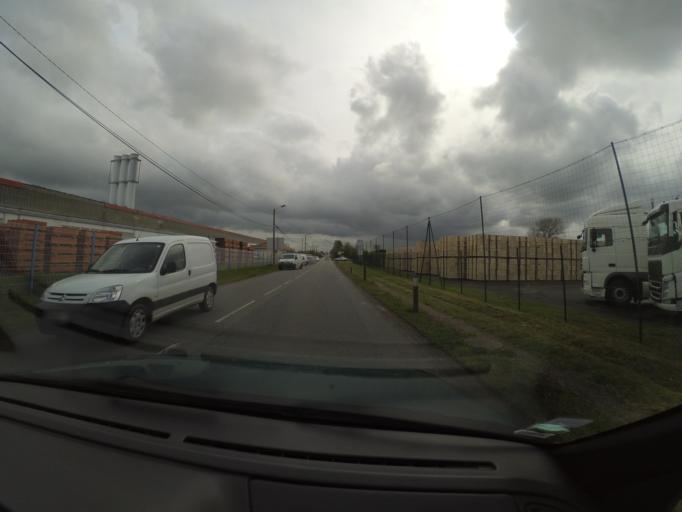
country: FR
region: Pays de la Loire
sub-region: Departement de la Loire-Atlantique
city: La Remaudiere
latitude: 47.2378
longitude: -1.2156
